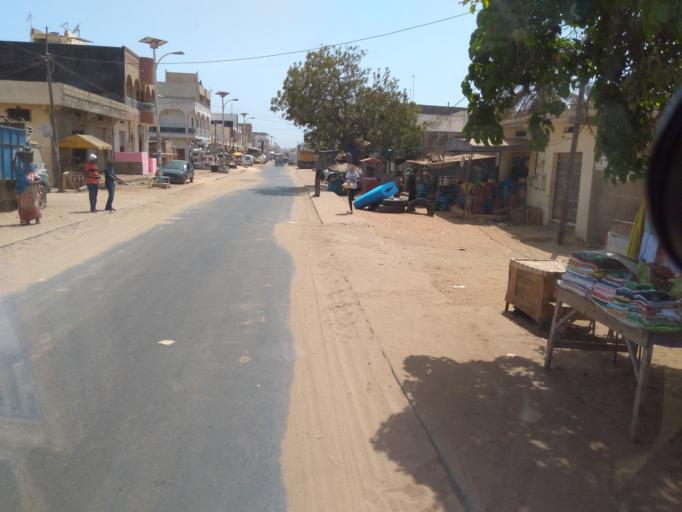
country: SN
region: Dakar
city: Pikine
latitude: 14.7878
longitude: -17.3456
